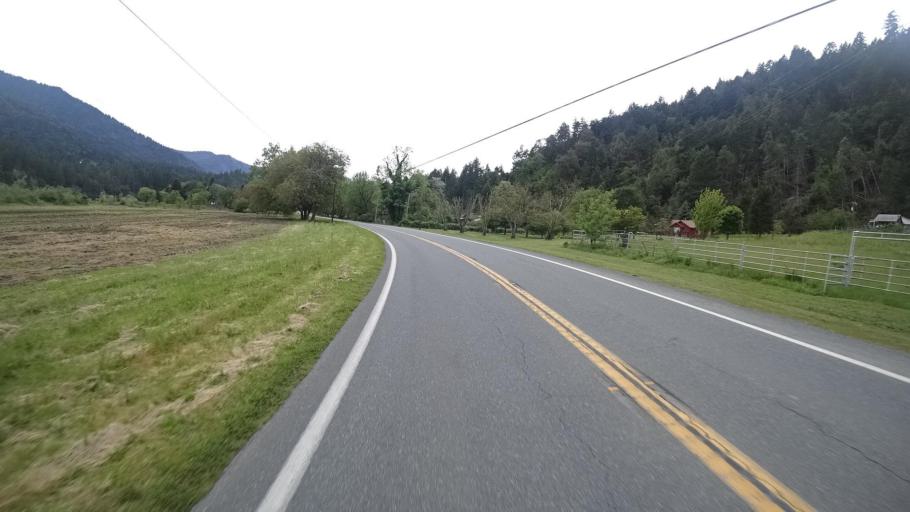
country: US
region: California
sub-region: Humboldt County
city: Willow Creek
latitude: 40.9775
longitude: -123.6418
